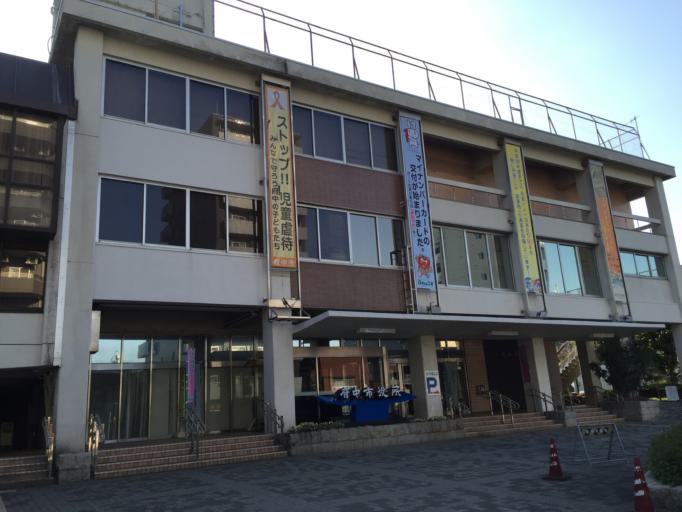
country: JP
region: Tokyo
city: Kokubunji
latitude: 35.6690
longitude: 139.4769
